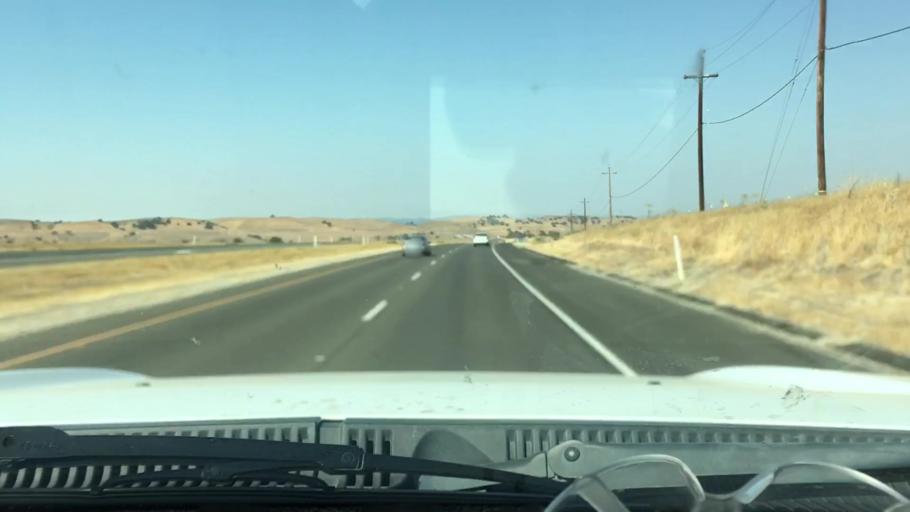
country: US
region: California
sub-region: San Luis Obispo County
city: Shandon
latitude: 35.6598
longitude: -120.4728
